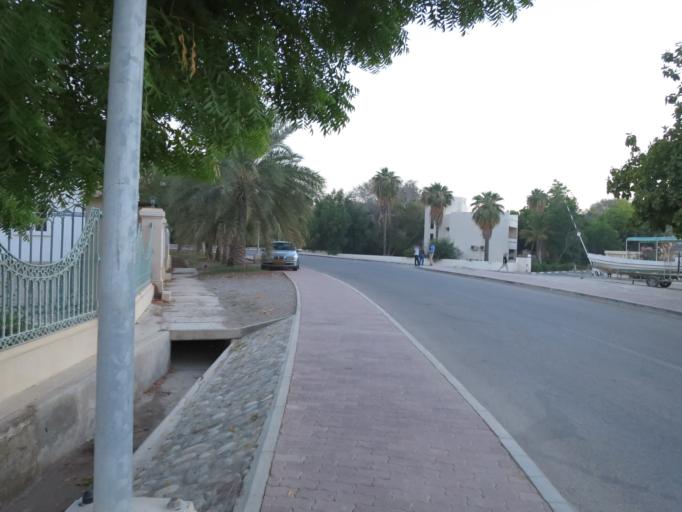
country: OM
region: Muhafazat Masqat
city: Bawshar
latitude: 23.6076
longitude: 58.4433
